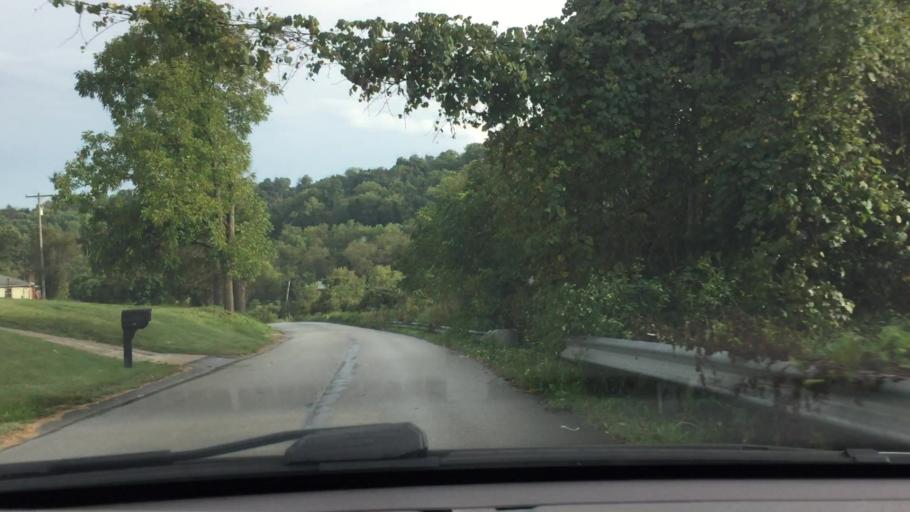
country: US
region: Pennsylvania
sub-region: Washington County
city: McGovern
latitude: 40.1859
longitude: -80.1651
